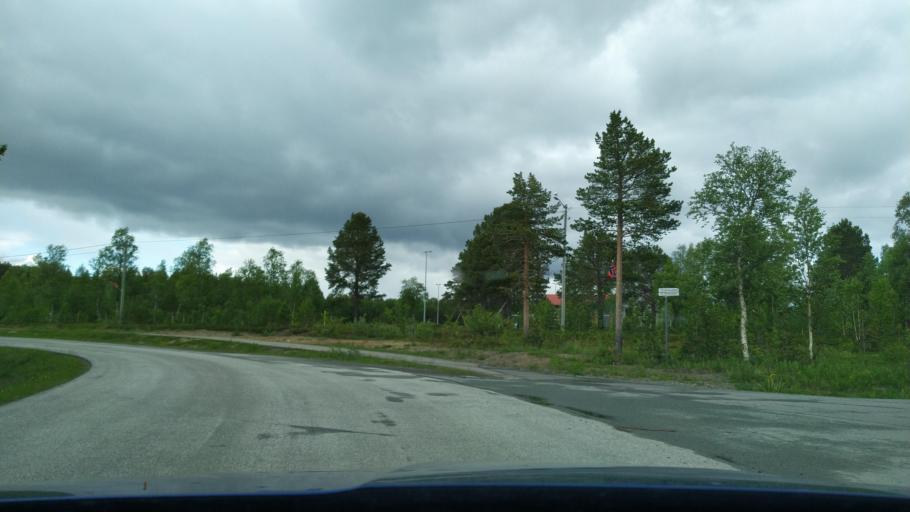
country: NO
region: Troms
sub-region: Dyroy
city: Brostadbotn
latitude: 69.0894
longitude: 17.7002
